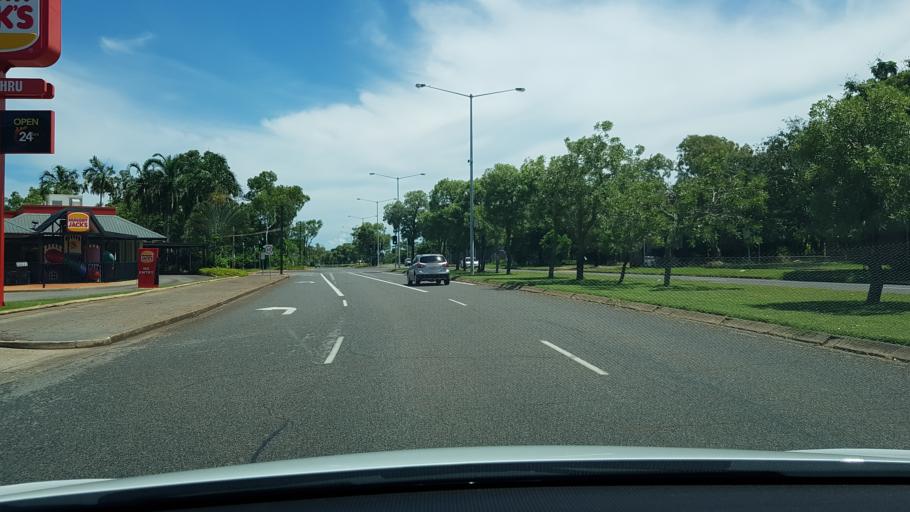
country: AU
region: Northern Territory
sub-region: Darwin
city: Leanyer
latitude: -12.3709
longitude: 130.8839
